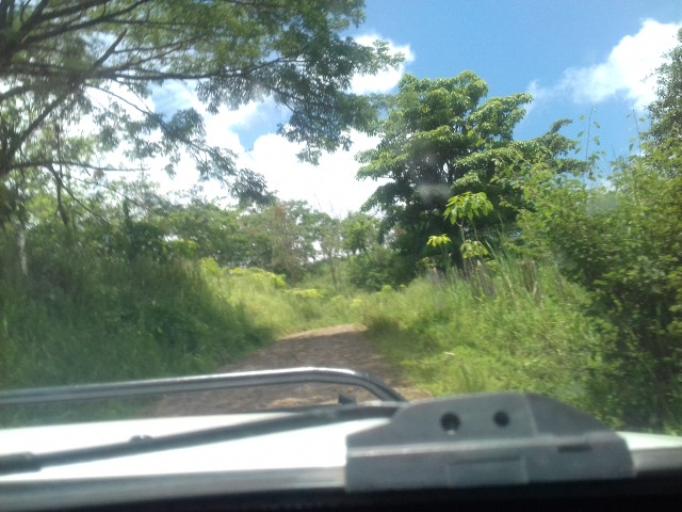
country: NI
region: Matagalpa
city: Matiguas
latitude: 13.0108
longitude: -85.3974
